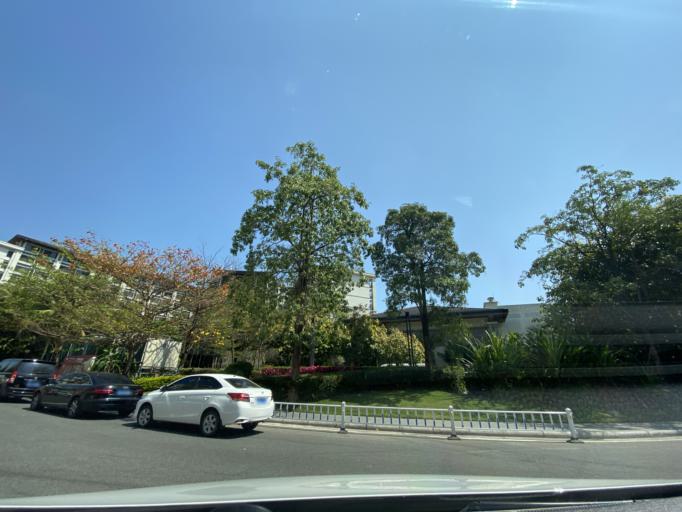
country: CN
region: Hainan
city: Yingzhou
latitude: 18.4046
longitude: 109.8456
